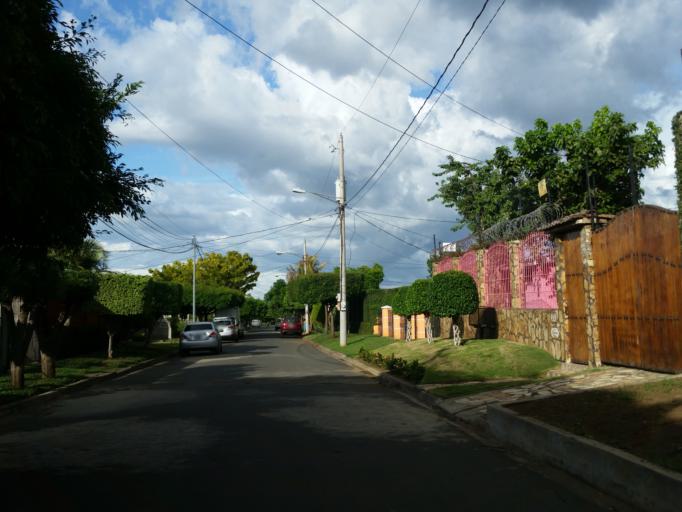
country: NI
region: Masaya
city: Ticuantepe
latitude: 12.0538
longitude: -86.1939
